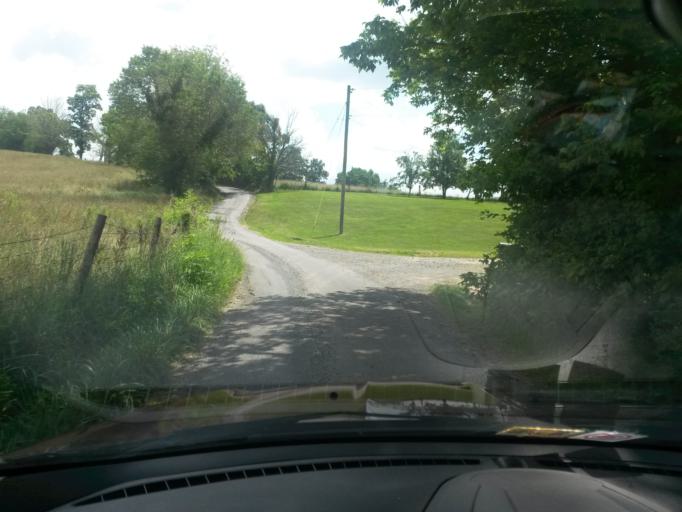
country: US
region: West Virginia
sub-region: Monroe County
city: Union
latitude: 37.5618
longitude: -80.5060
